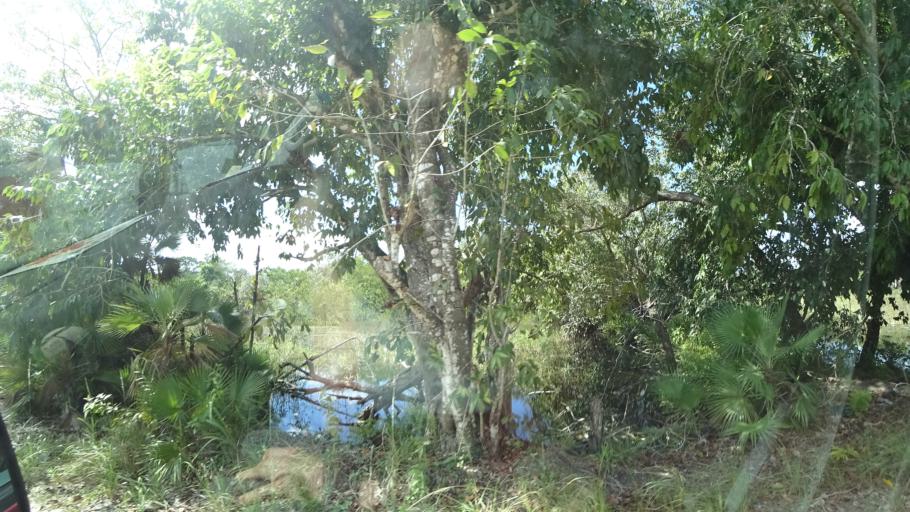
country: BZ
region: Belize
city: Belize City
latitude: 17.5711
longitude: -88.4142
